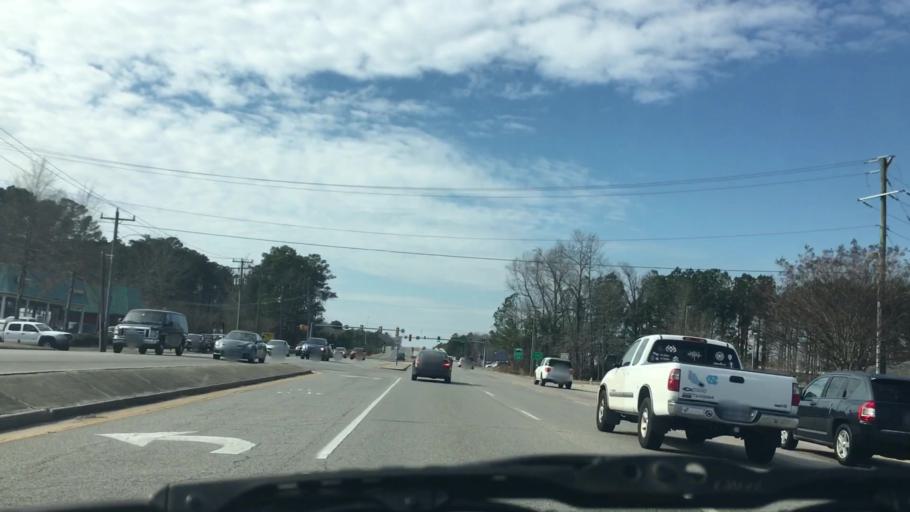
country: US
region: Virginia
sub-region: City of Portsmouth
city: Portsmouth Heights
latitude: 36.8655
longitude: -76.4203
